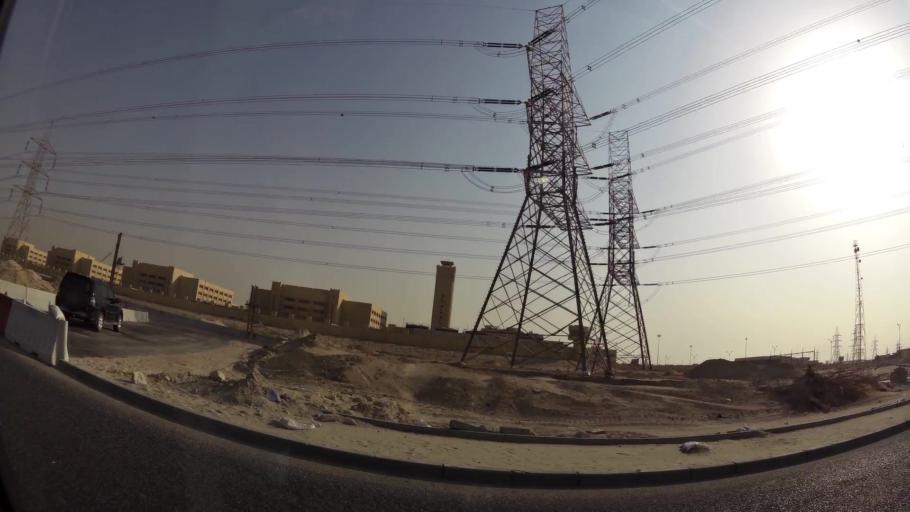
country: KW
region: Al Asimah
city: Ar Rabiyah
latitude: 29.2950
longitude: 47.8561
